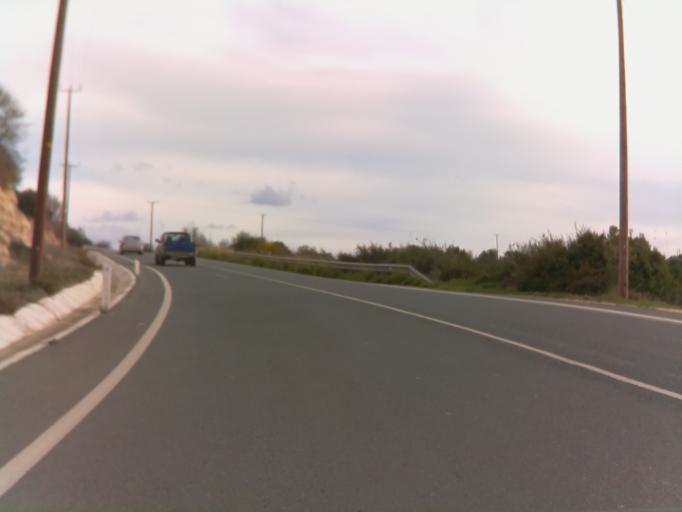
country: CY
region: Pafos
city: Polis
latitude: 34.9925
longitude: 32.4048
